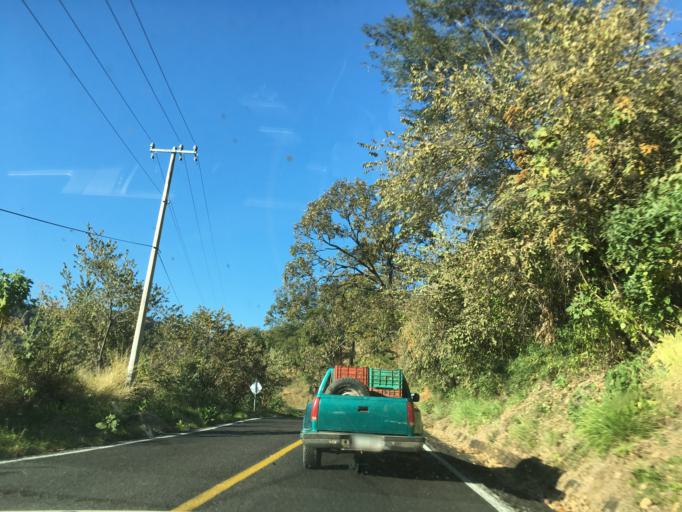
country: MX
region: Michoacan
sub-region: Uruapan
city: Santa Rosa (Santa Barbara)
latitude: 19.3103
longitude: -102.0707
